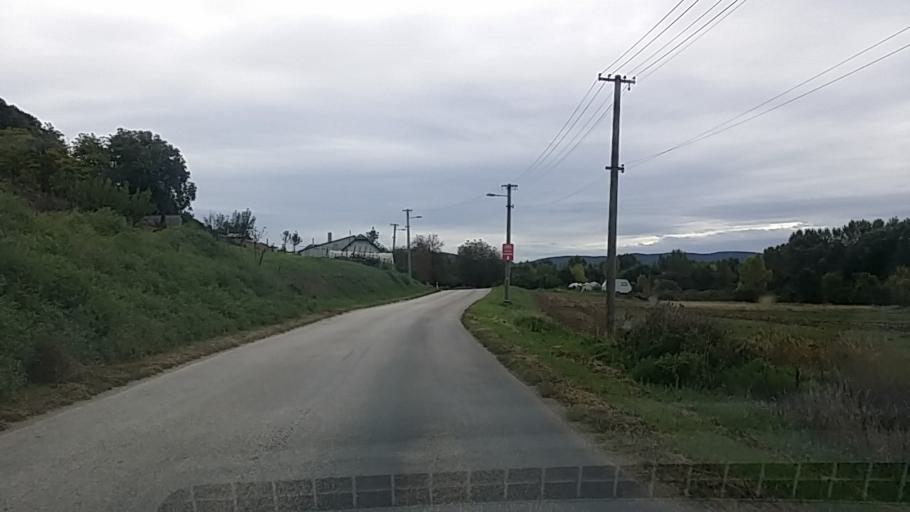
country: HU
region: Komarom-Esztergom
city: Esztergom
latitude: 47.8262
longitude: 18.7415
